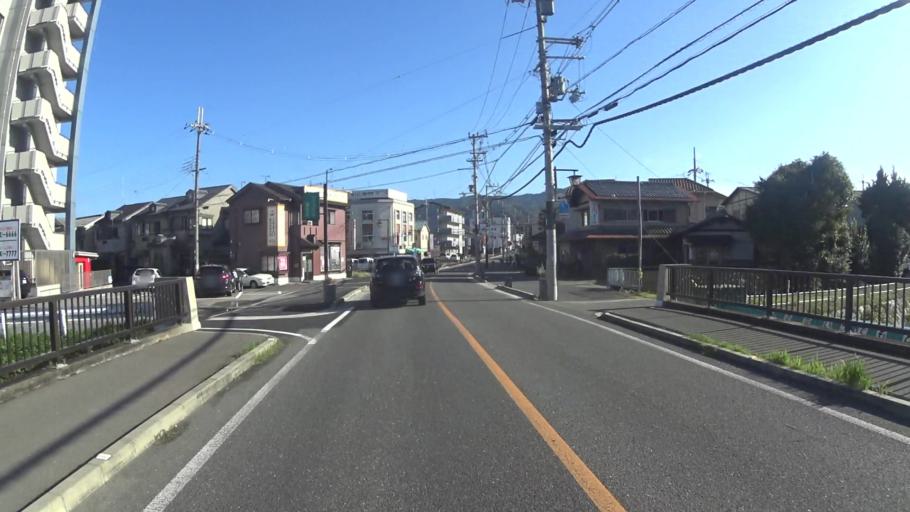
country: JP
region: Kyoto
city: Kameoka
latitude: 35.0070
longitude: 135.5896
